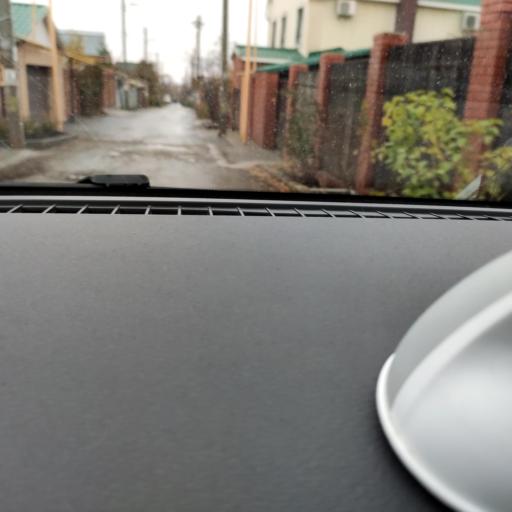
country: RU
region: Samara
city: Samara
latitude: 53.2708
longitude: 50.2133
